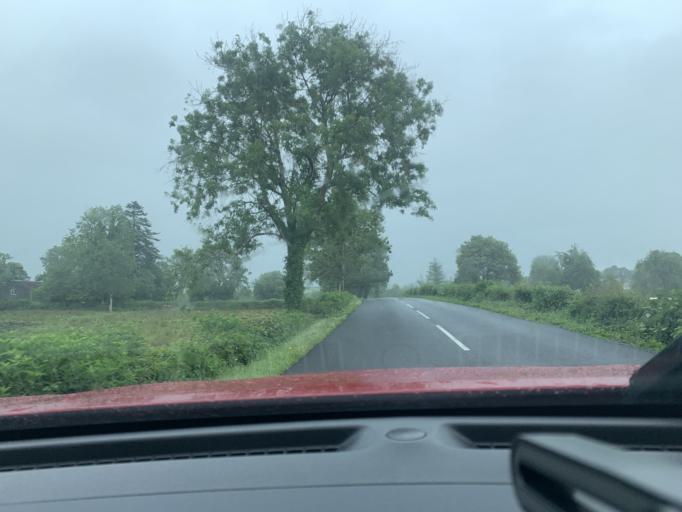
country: GB
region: Northern Ireland
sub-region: Fermanagh District
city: Enniskillen
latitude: 54.2924
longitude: -7.6972
